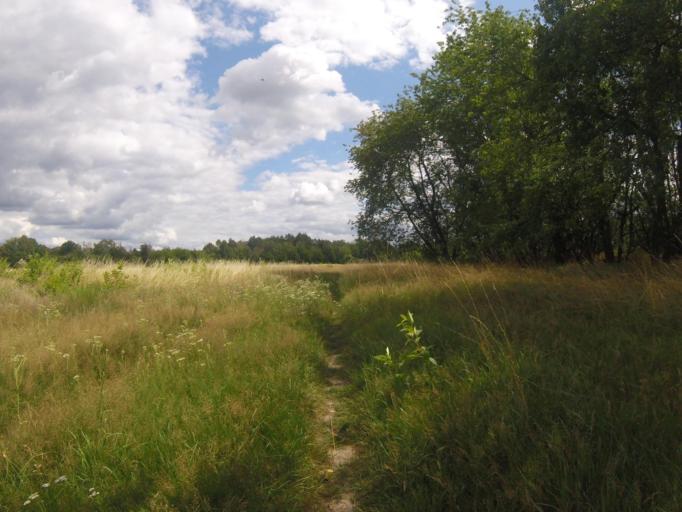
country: DE
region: Brandenburg
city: Konigs Wusterhausen
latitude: 52.3084
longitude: 13.6131
